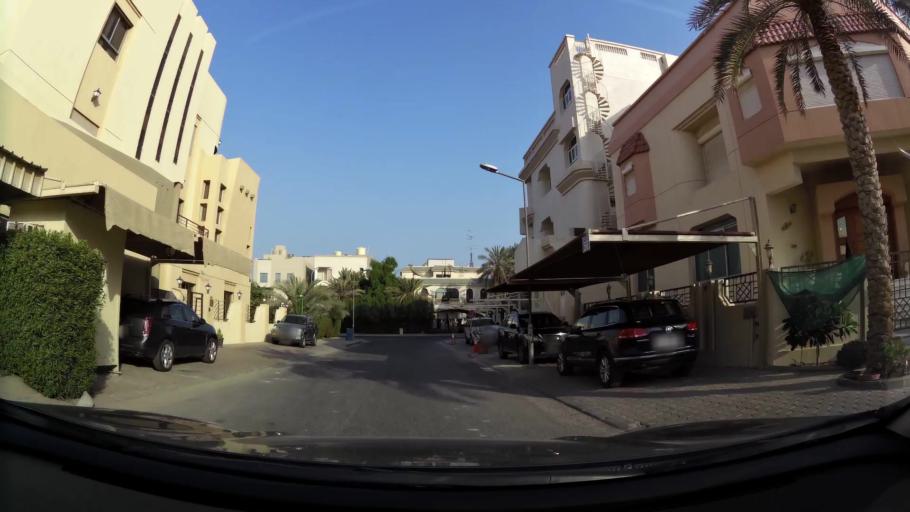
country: KW
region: Muhafazat Hawalli
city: Ar Rumaythiyah
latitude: 29.3193
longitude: 48.0815
